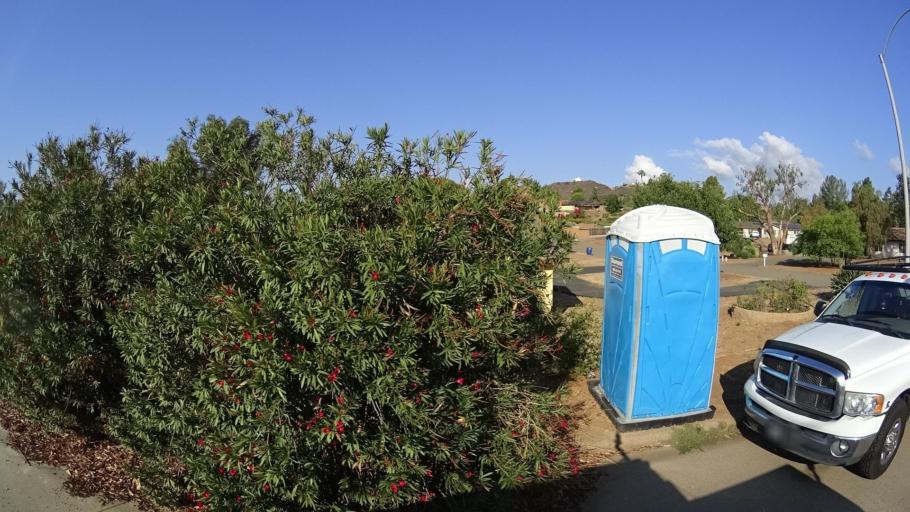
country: US
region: California
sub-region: San Diego County
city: Eucalyptus Hills
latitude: 32.8810
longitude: -116.9418
